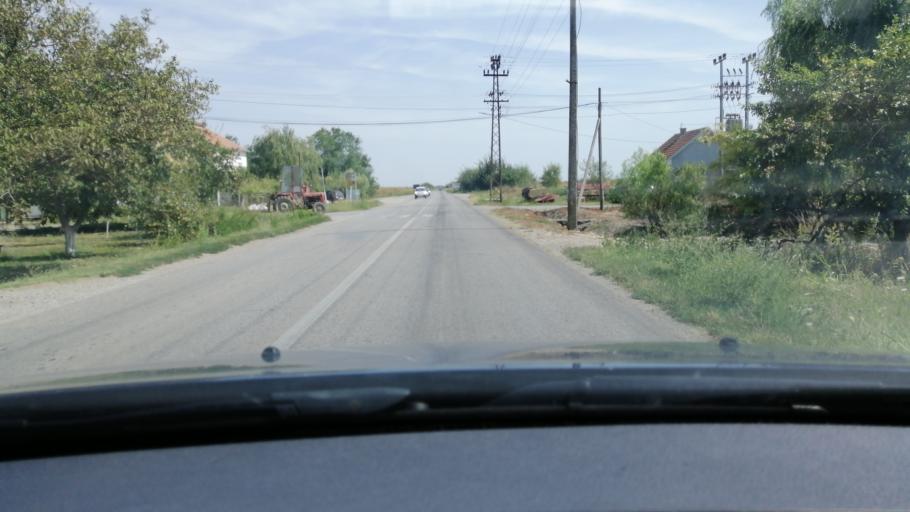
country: RS
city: Sutjeska
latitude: 45.3807
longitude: 20.7017
